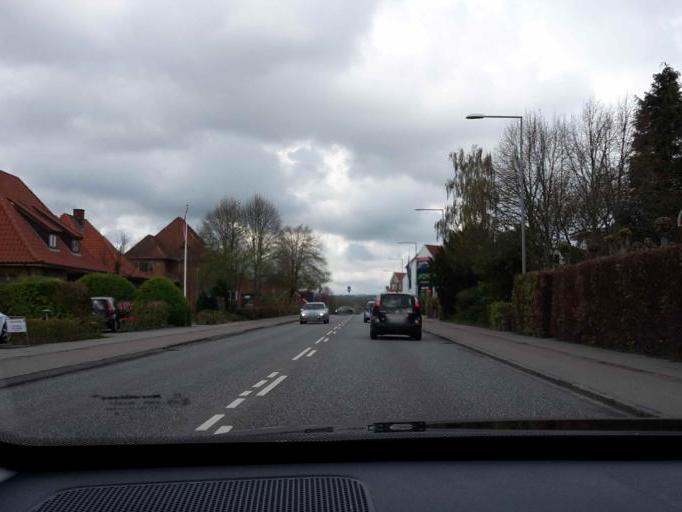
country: DK
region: South Denmark
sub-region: Vejle Kommune
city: Vejle
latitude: 55.6939
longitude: 9.5442
